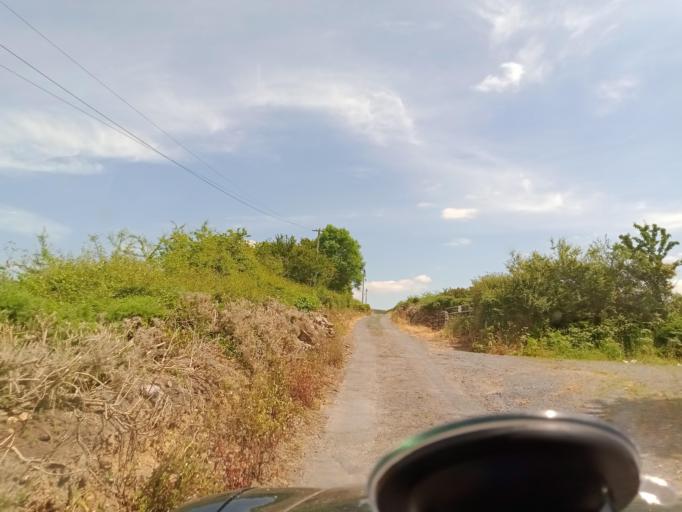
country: IE
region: Leinster
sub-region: Kilkenny
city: Thomastown
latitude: 52.5666
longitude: -7.0868
